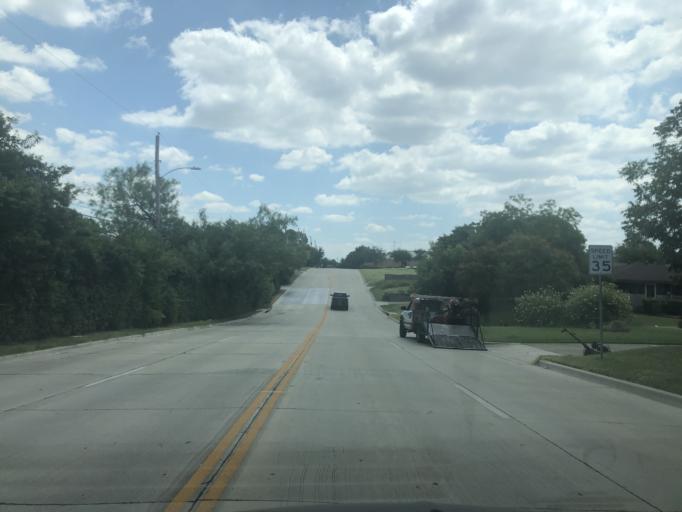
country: US
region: Texas
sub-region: Dallas County
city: Grand Prairie
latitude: 32.7488
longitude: -97.0099
